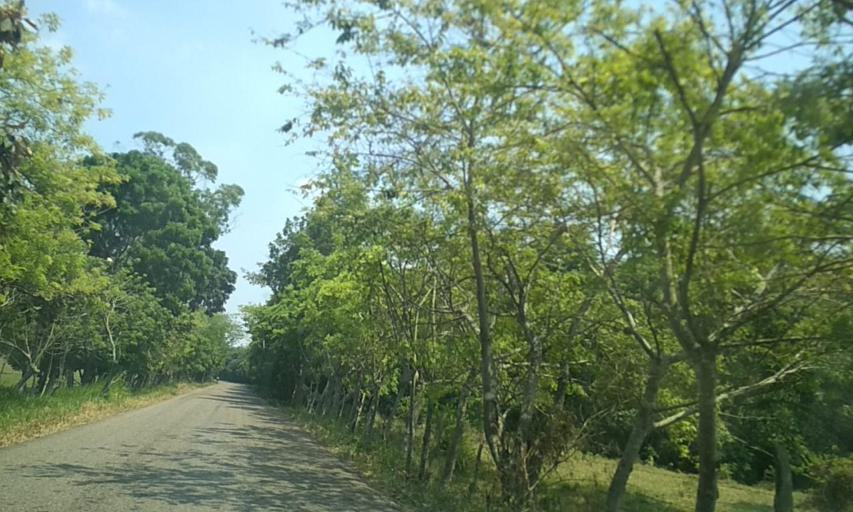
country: MX
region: Tabasco
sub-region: Huimanguillo
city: C-41 (Licenciado Carlos A. Madrazo)
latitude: 17.8403
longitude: -93.5209
